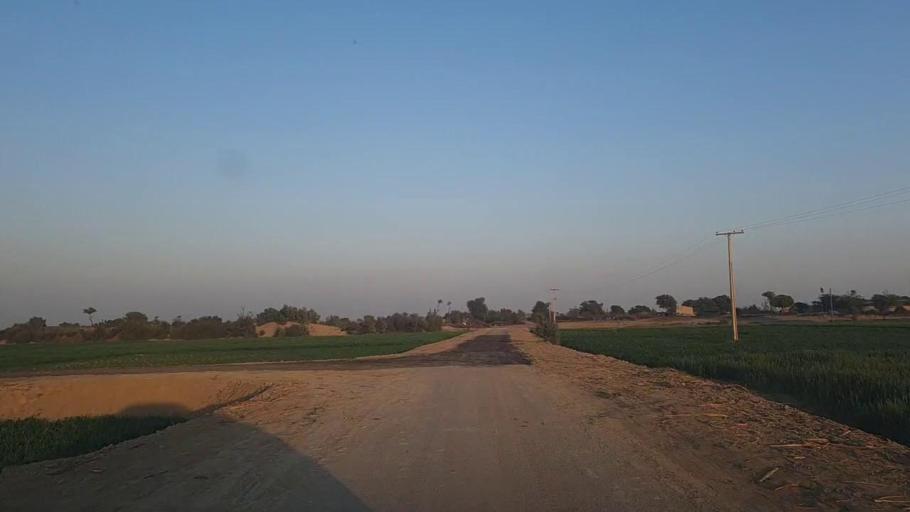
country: PK
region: Sindh
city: Jam Sahib
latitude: 26.3525
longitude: 68.7183
